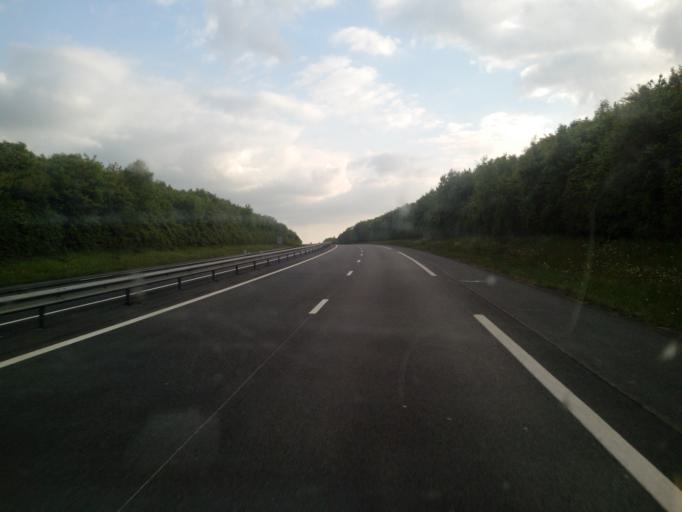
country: FR
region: Lower Normandy
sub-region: Departement du Calvados
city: Saint-Martin-des-Besaces
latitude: 49.0071
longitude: -0.9021
